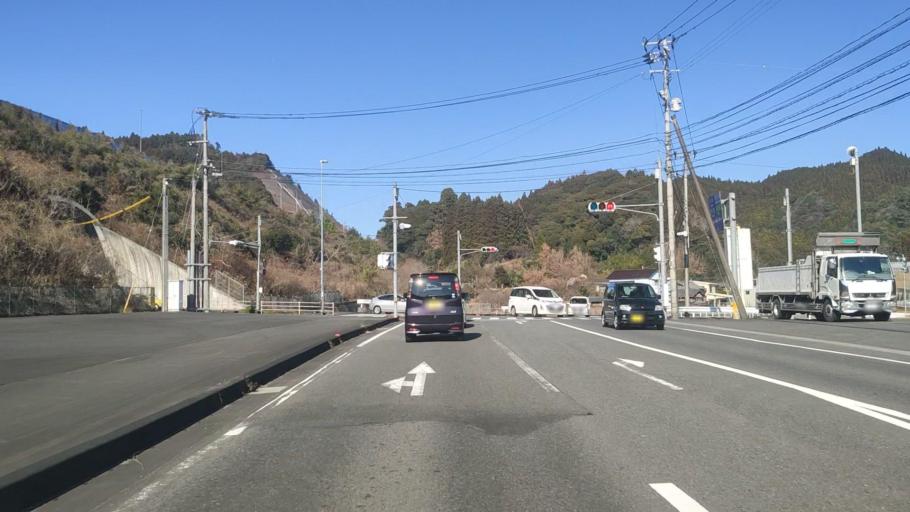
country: JP
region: Oita
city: Saiki
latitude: 32.9735
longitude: 131.8635
